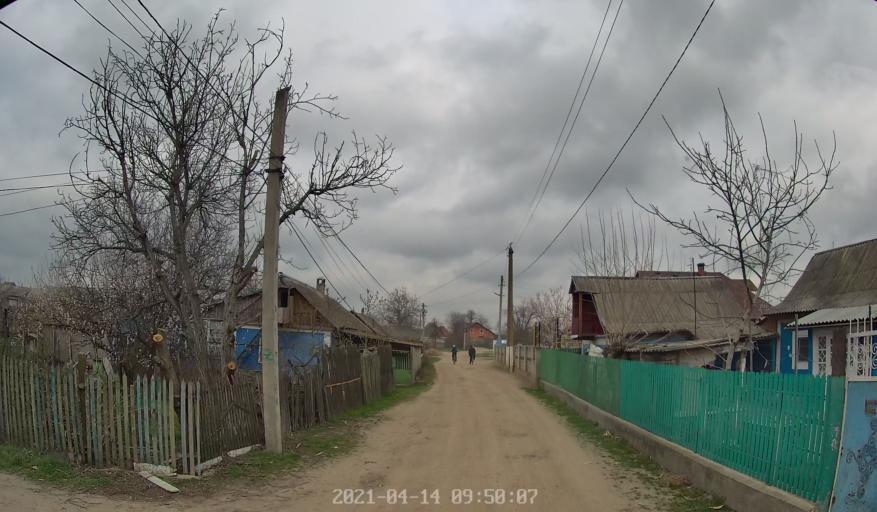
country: MD
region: Chisinau
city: Vadul lui Voda
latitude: 47.1403
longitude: 29.1250
